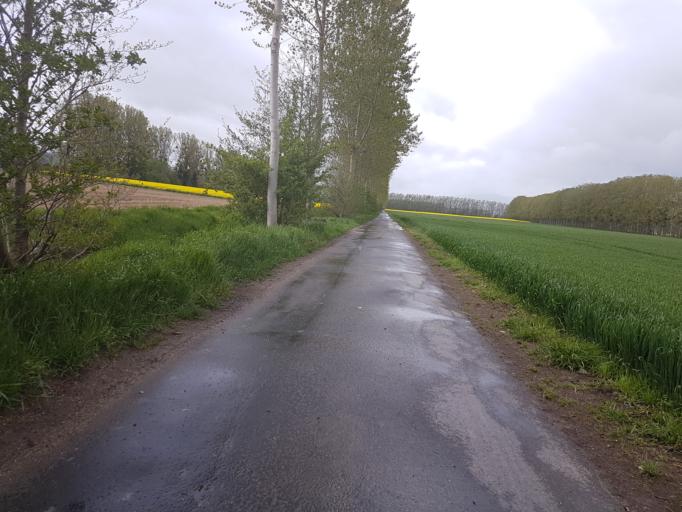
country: CH
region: Vaud
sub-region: Jura-Nord vaudois District
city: Yverdon-les-Bains
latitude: 46.7625
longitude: 6.6203
